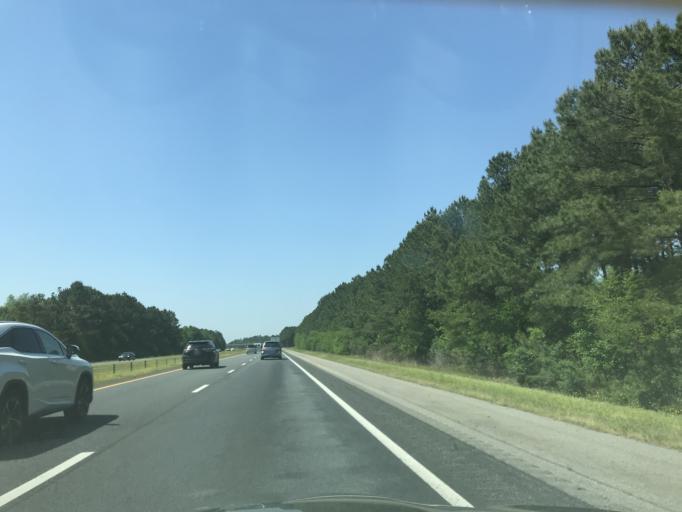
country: US
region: North Carolina
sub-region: Johnston County
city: Benson
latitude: 35.3602
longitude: -78.4868
